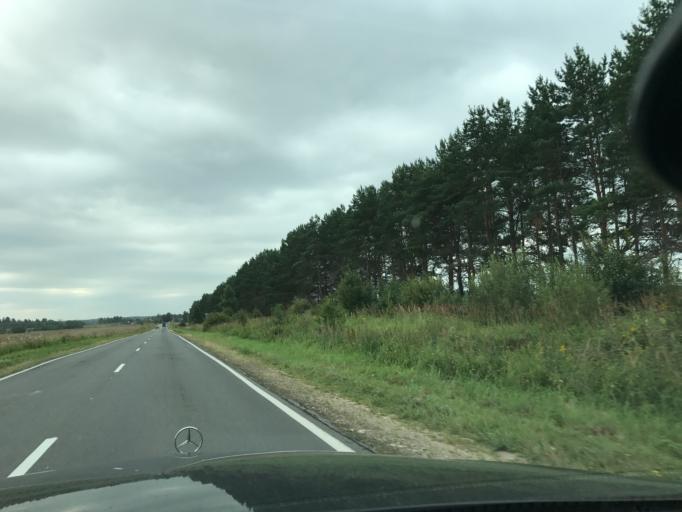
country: RU
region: Vladimir
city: Galitsy
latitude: 56.1684
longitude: 42.8123
